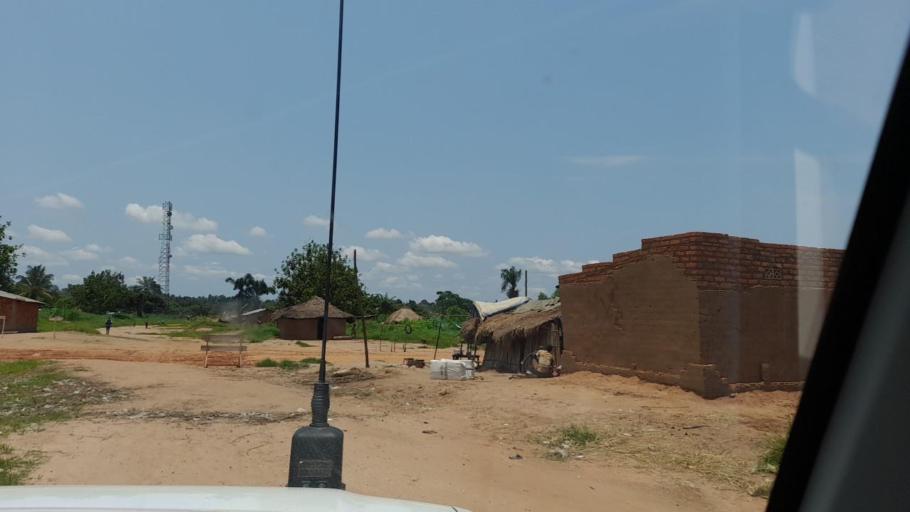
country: CD
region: Kasai-Occidental
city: Kananga
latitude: -5.9523
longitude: 22.2775
